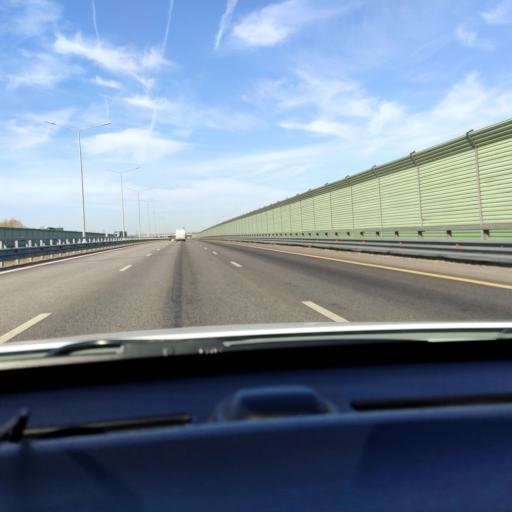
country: RU
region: Voronezj
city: Ramon'
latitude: 51.8177
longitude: 39.2513
